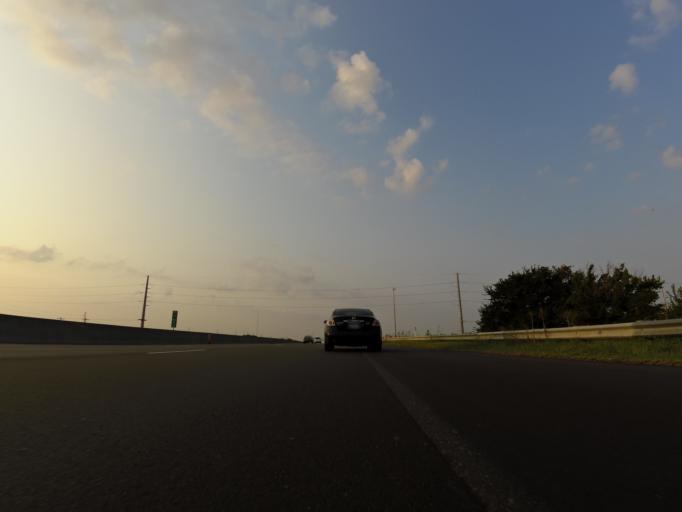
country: US
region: Kansas
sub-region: Sedgwick County
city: Park City
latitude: 37.7532
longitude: -97.3200
